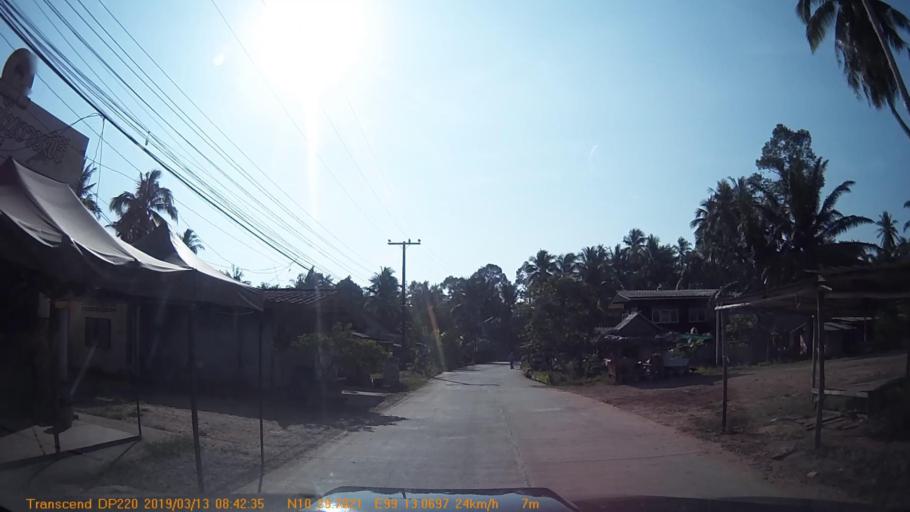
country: TH
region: Chumphon
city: Chumphon
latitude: 10.4963
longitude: 99.2179
